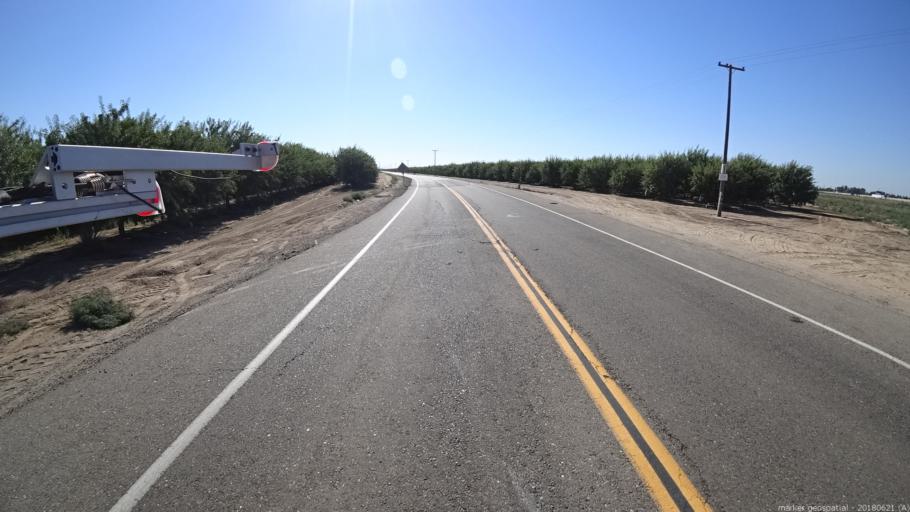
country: US
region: California
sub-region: Fresno County
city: Biola
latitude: 36.8514
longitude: -119.9415
